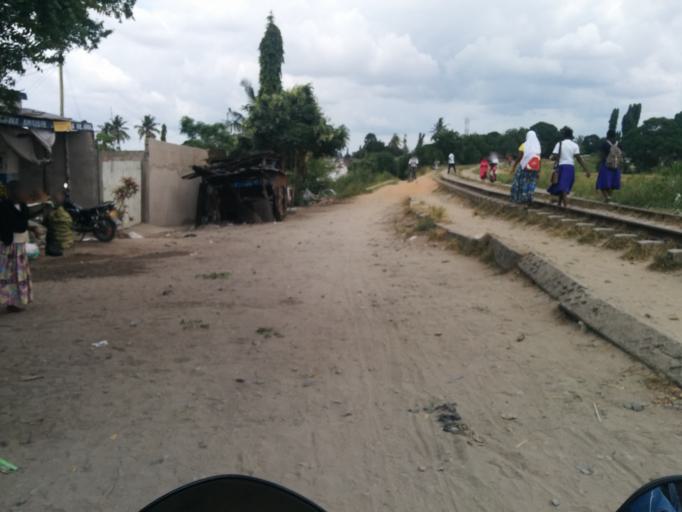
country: TZ
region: Dar es Salaam
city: Dar es Salaam
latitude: -6.8625
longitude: 39.2457
